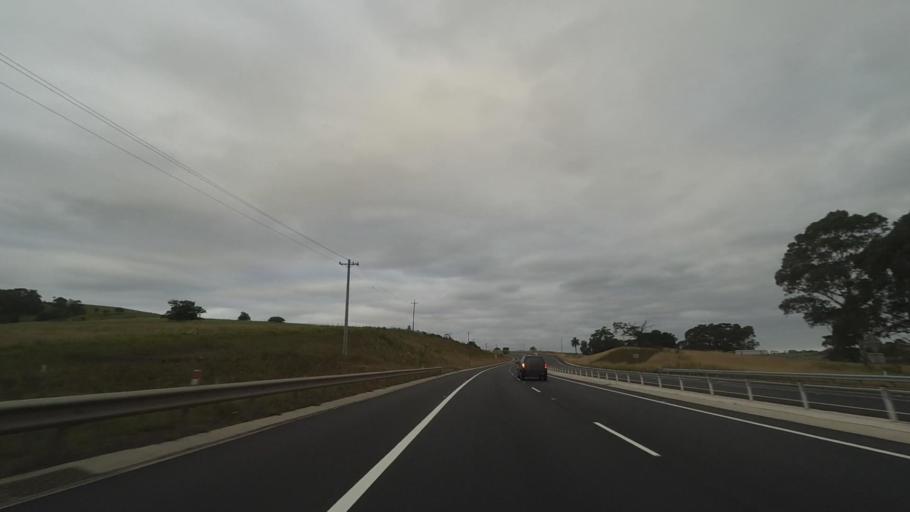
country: AU
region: New South Wales
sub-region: Kiama
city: Gerringong
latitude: -34.7494
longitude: 150.7925
